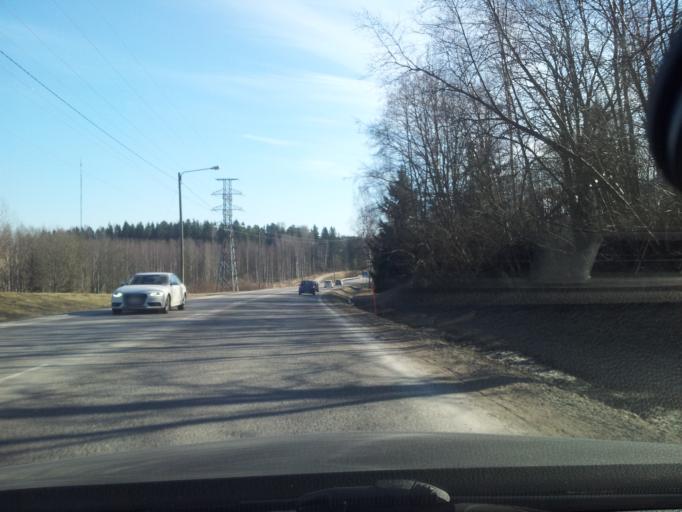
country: FI
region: Uusimaa
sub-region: Helsinki
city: Espoo
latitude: 60.1832
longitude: 24.6047
